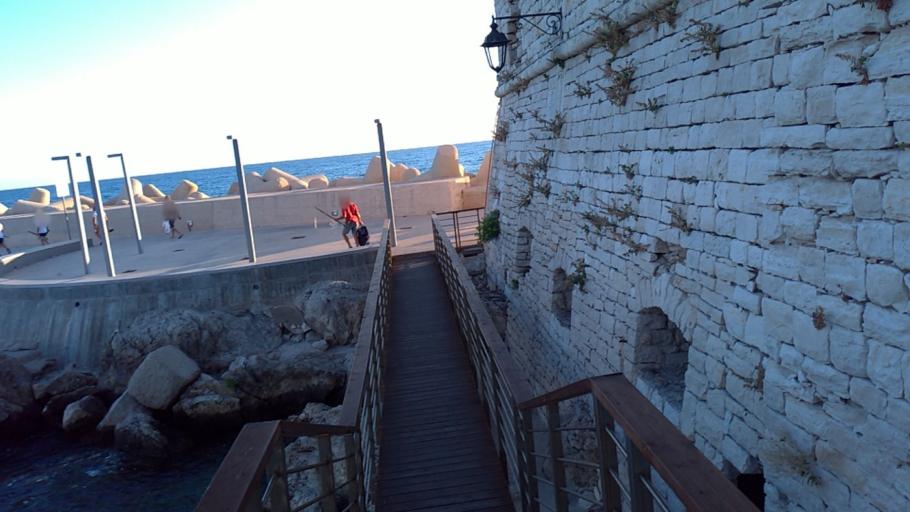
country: IT
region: Apulia
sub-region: Provincia di Bari
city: Giovinazzo
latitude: 41.1903
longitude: 16.6739
